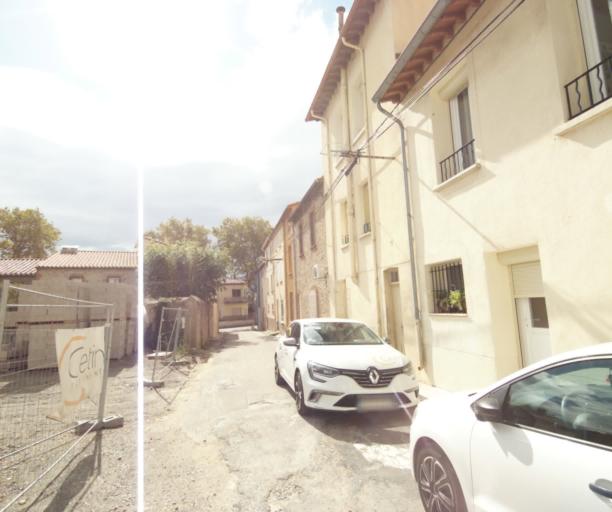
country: FR
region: Languedoc-Roussillon
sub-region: Departement des Pyrenees-Orientales
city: Argelers
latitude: 42.5478
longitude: 3.0270
